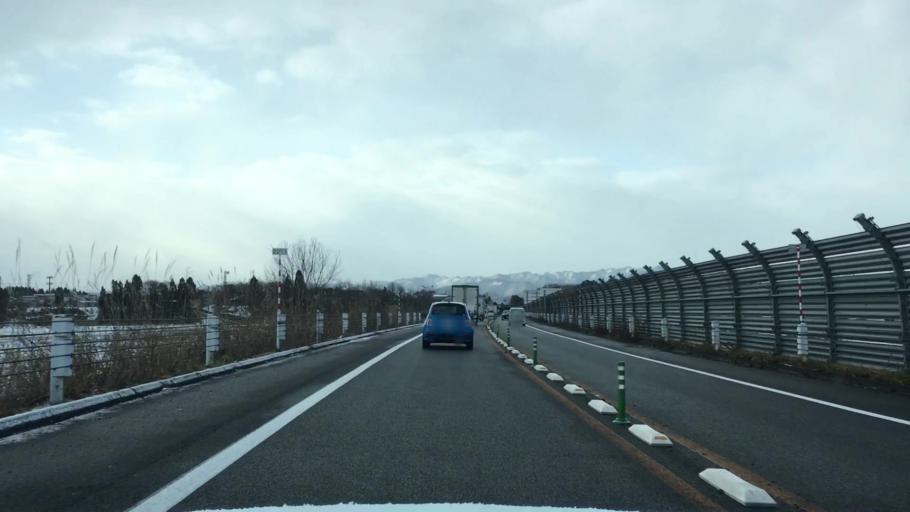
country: JP
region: Akita
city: Odate
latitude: 40.2815
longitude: 140.5393
